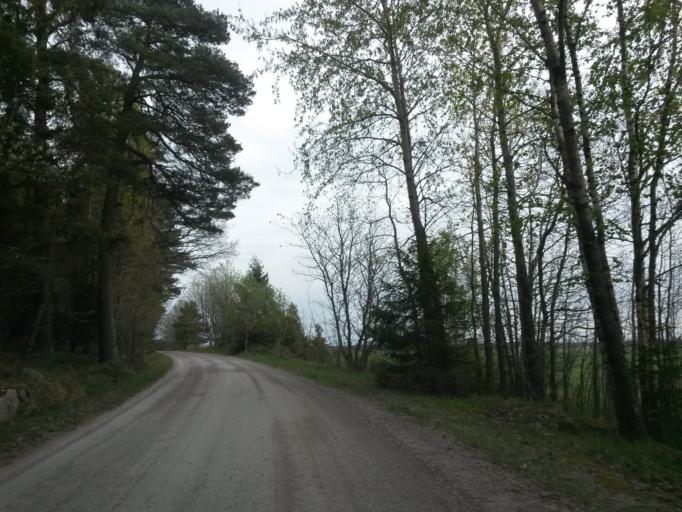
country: SE
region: Vaestra Goetaland
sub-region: Grastorps Kommun
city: Graestorp
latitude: 58.3770
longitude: 12.8015
